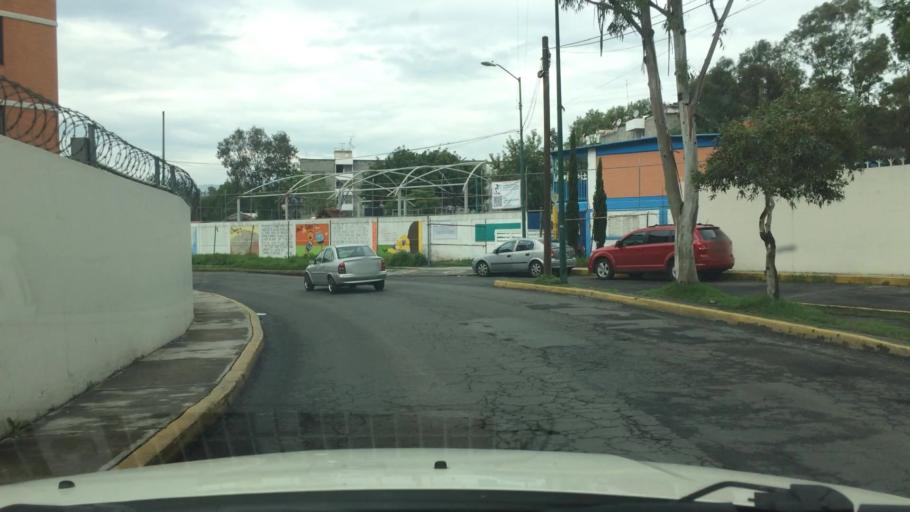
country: MX
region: Mexico City
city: Xochimilco
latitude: 19.2961
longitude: -99.1022
